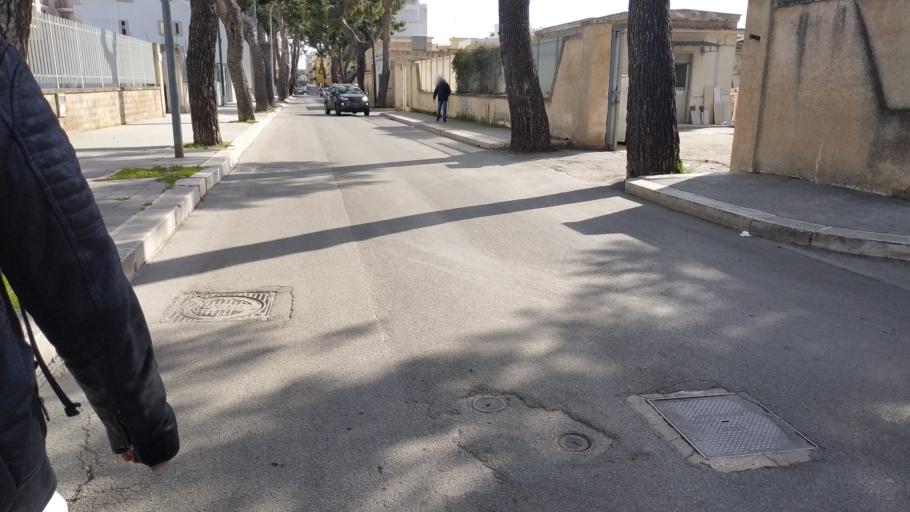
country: IT
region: Apulia
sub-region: Provincia di Bari
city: Bitonto
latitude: 41.1078
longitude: 16.6807
